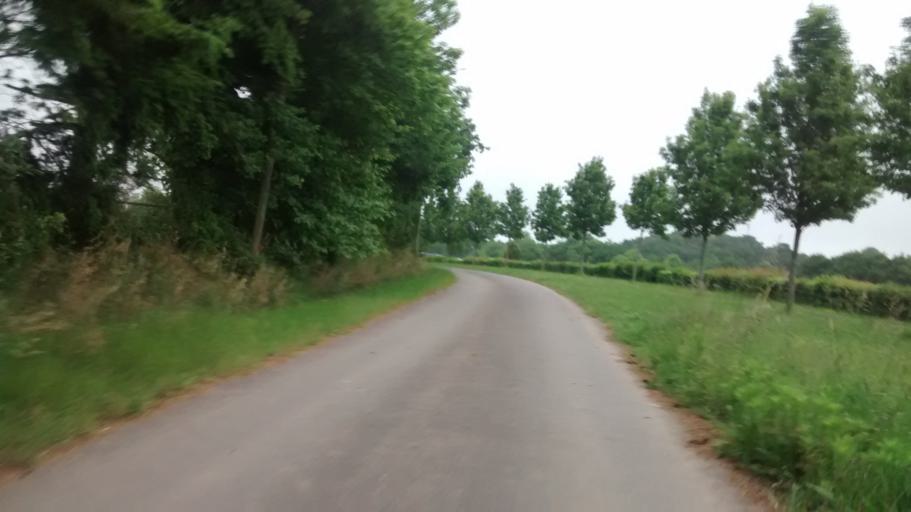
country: FR
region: Brittany
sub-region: Departement du Morbihan
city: Malestroit
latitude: 47.7992
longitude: -2.3998
